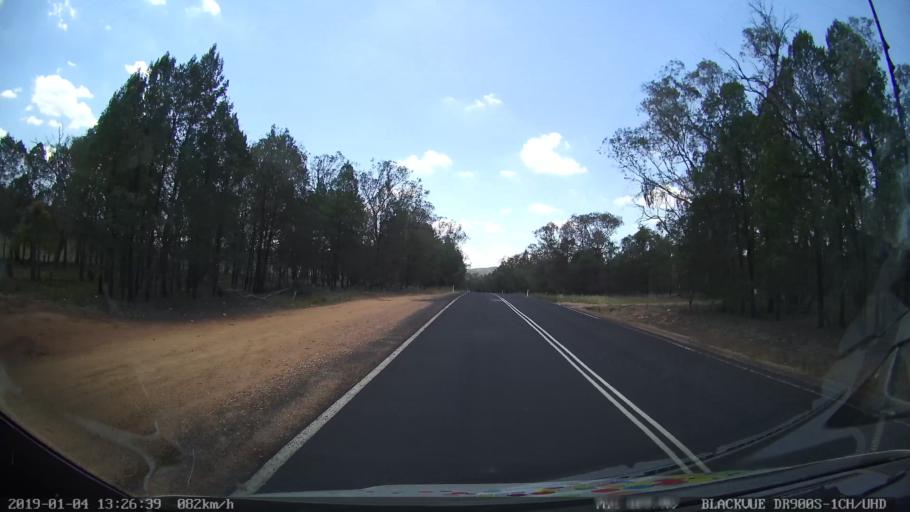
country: AU
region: New South Wales
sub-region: Parkes
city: Peak Hill
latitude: -32.6788
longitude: 148.5590
